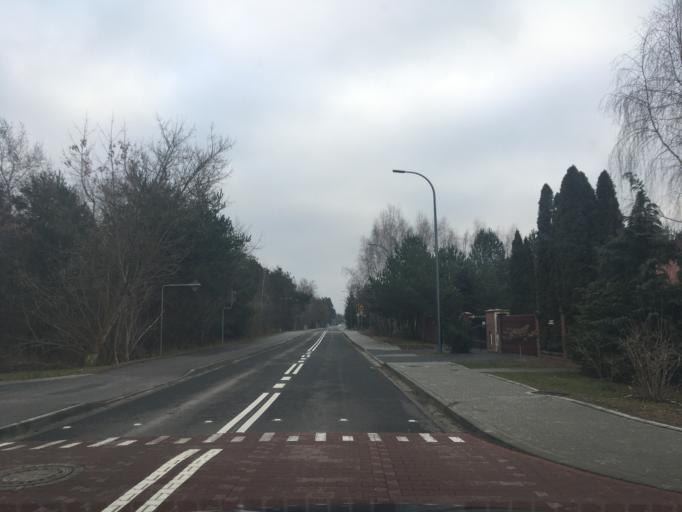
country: PL
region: Masovian Voivodeship
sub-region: Powiat piaseczynski
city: Lesznowola
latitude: 52.0655
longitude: 20.9745
